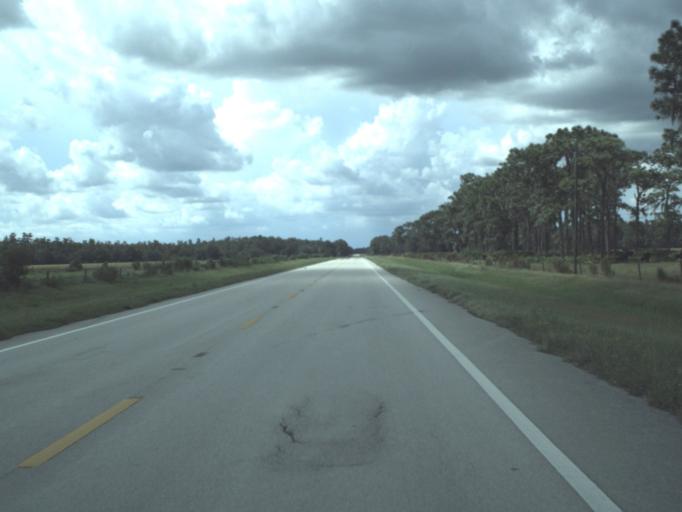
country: US
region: Florida
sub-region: Hardee County
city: Zolfo Springs
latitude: 27.4437
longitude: -81.6186
